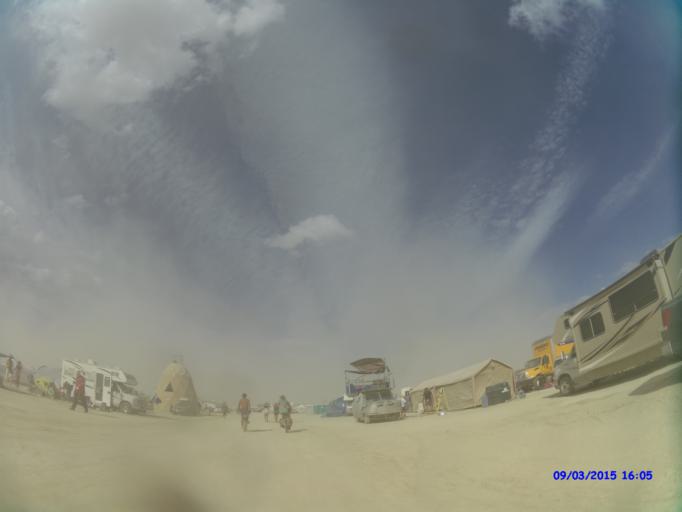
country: US
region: Nevada
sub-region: Pershing County
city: Lovelock
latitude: 40.7812
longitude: -119.1962
